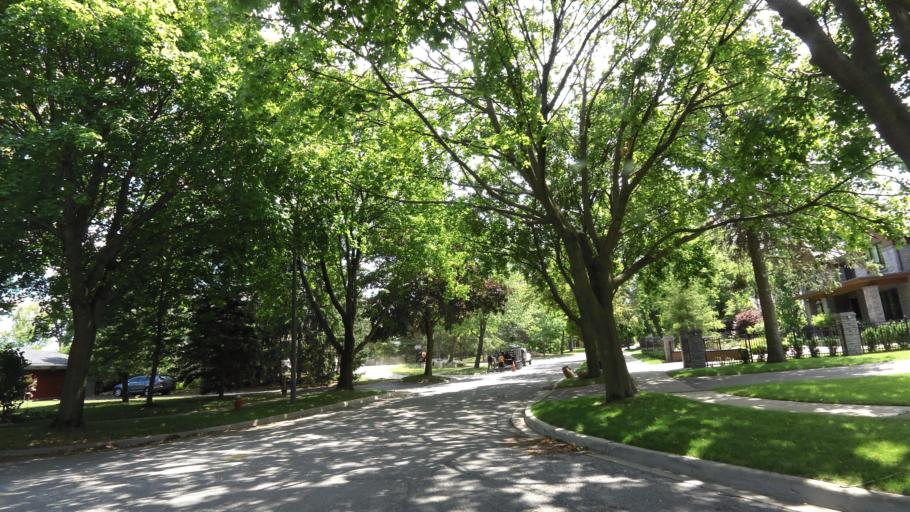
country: CA
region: Ontario
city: Mississauga
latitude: 43.5160
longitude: -79.6031
